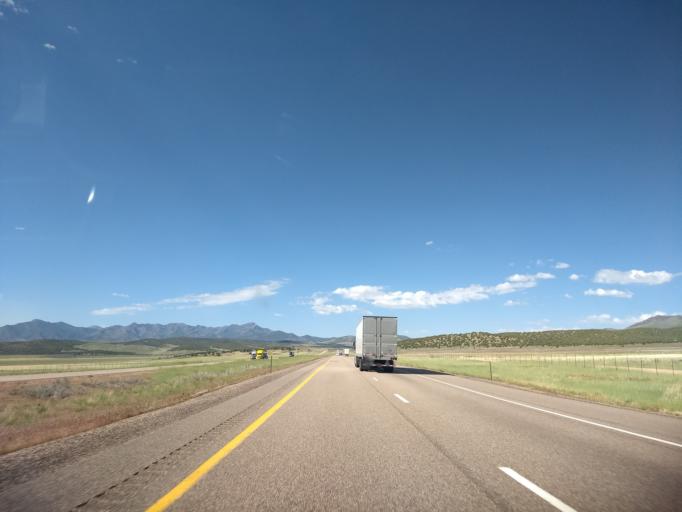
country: US
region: Utah
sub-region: Millard County
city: Fillmore
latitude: 39.1237
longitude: -112.2467
